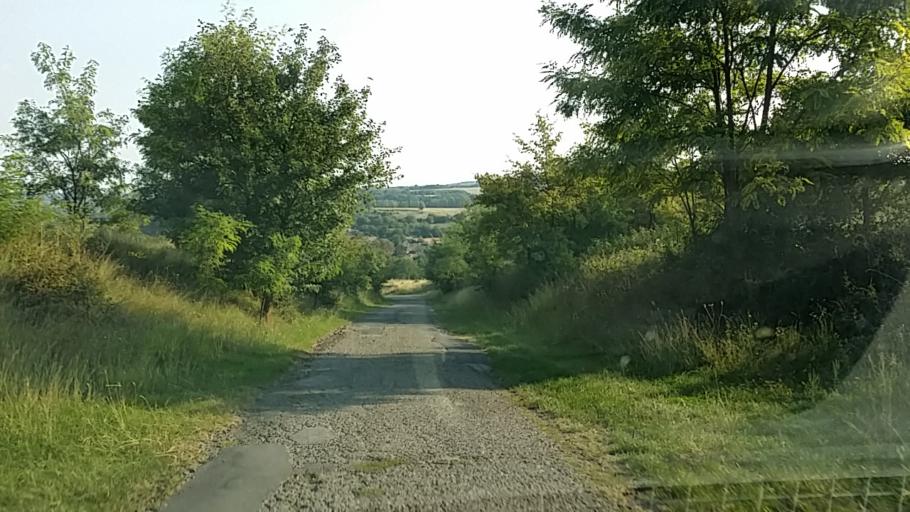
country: HU
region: Nograd
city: Bujak
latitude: 47.8698
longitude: 19.5006
